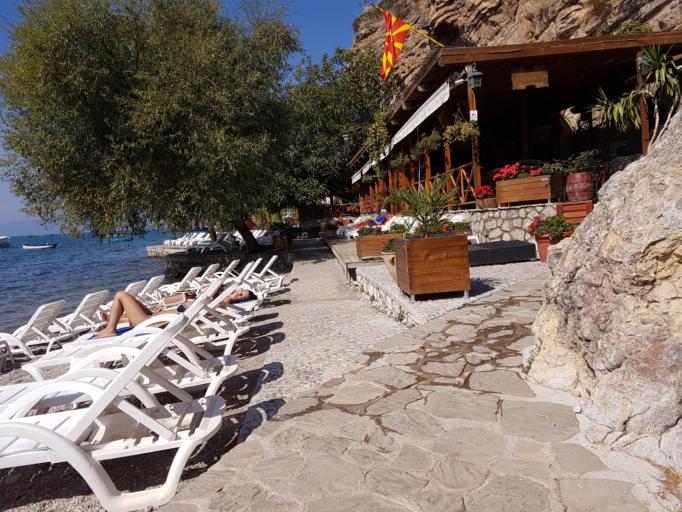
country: MK
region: Ohrid
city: Ohrid
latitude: 41.1107
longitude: 20.7920
